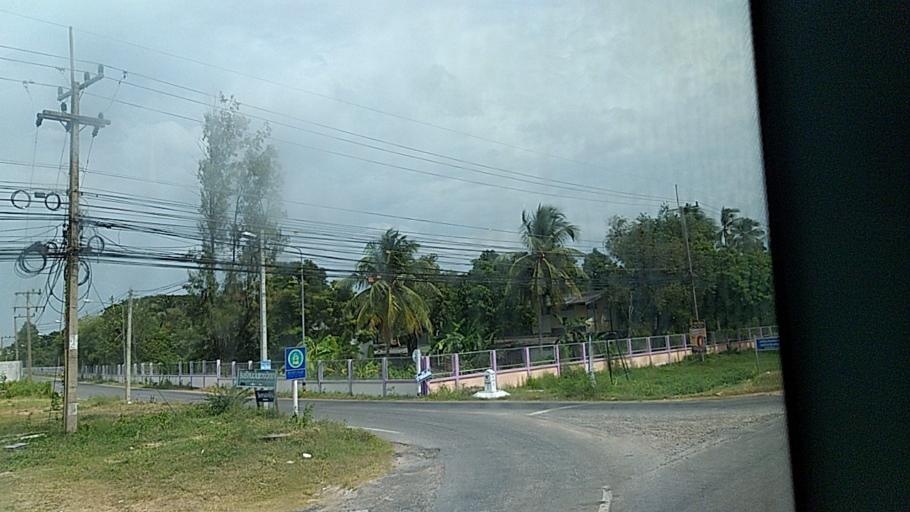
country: TH
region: Roi Et
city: Roi Et
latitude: 16.0712
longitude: 103.6001
